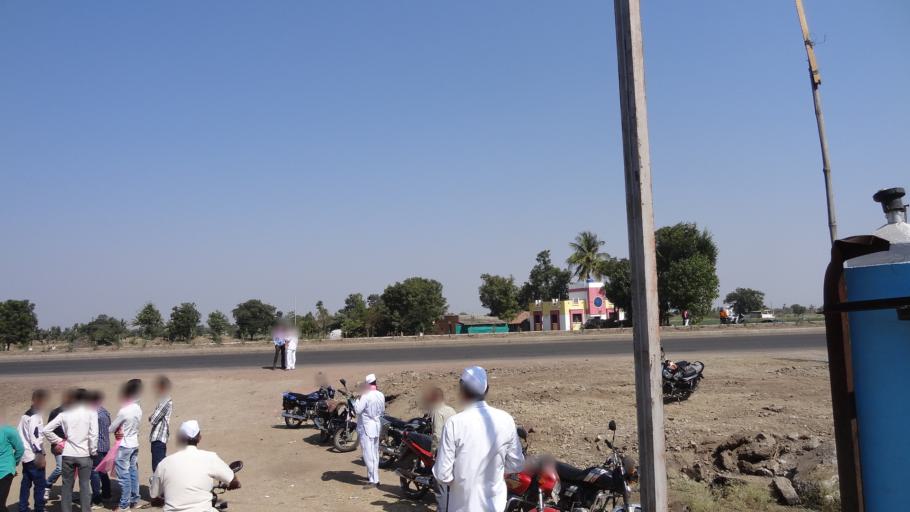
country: IN
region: Maharashtra
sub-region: Nashik Division
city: Sinnar
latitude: 19.7341
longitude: 74.1232
